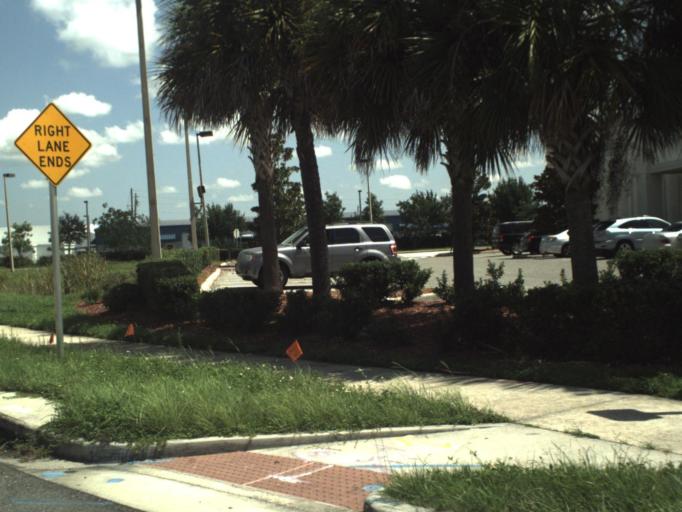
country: US
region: Florida
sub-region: Orange County
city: Conway
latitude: 28.4662
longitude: -81.2759
